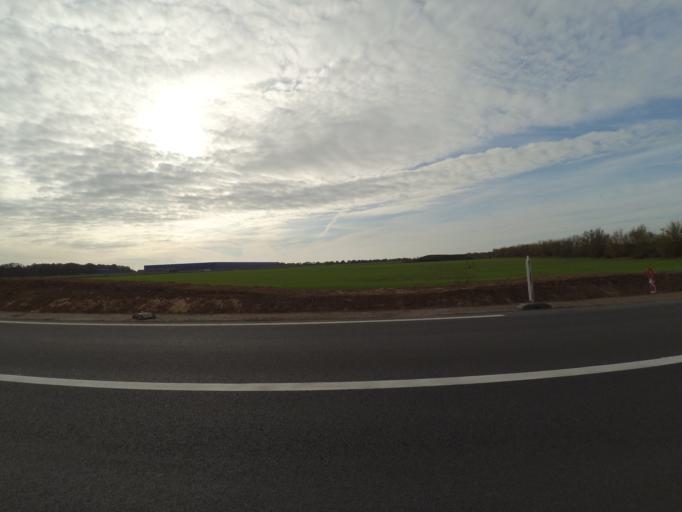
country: FR
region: Pays de la Loire
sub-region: Departement de la Vendee
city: Saint-Hilaire-de-Loulay
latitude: 47.0251
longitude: -1.3485
